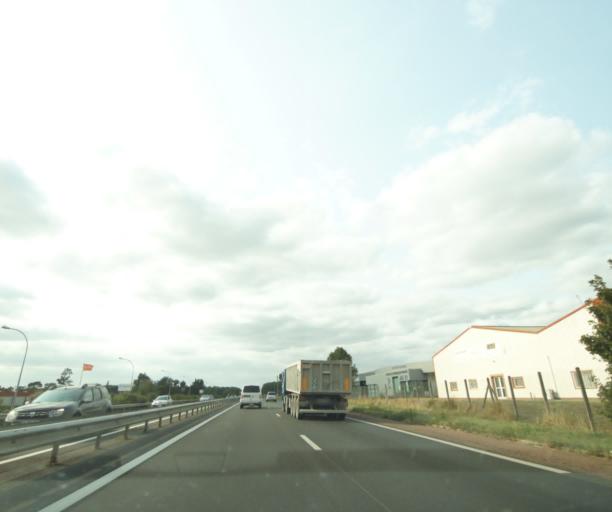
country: FR
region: Centre
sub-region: Departement d'Indre-et-Loire
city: Esvres
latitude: 47.3010
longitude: 0.7967
